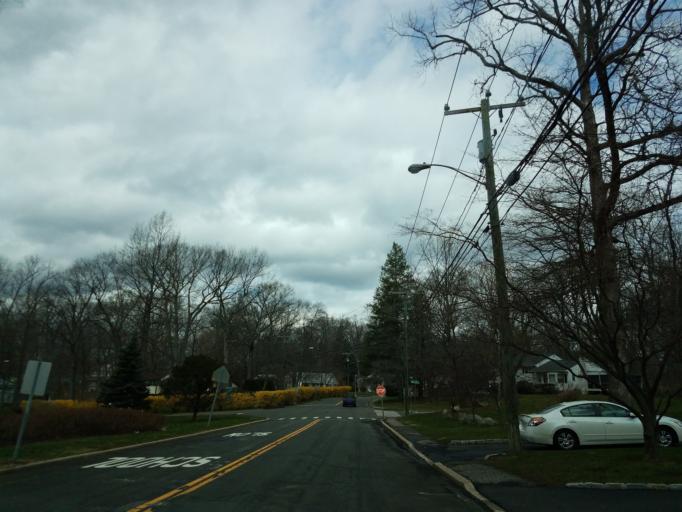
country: US
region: Connecticut
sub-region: Fairfield County
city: Stamford
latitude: 41.0920
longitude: -73.5409
